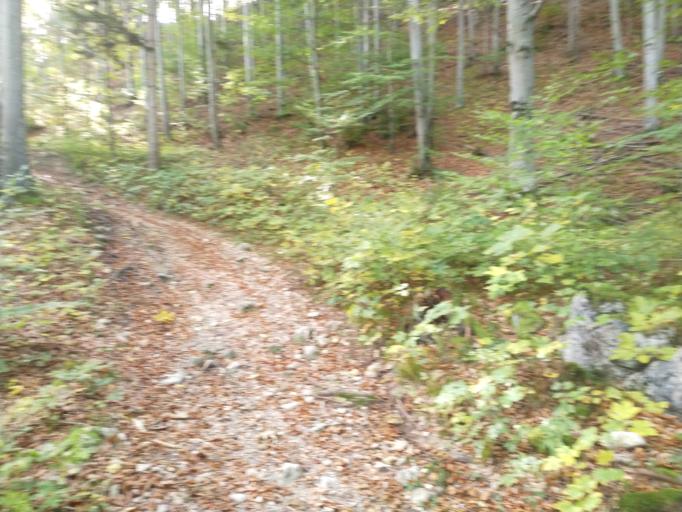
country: AT
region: Tyrol
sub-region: Politischer Bezirk Reutte
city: Vils
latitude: 47.5635
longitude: 10.6558
